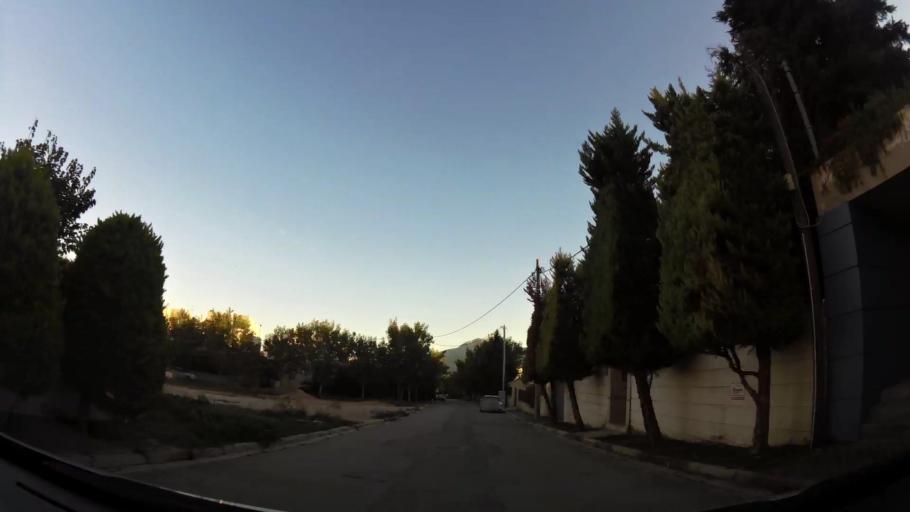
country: GR
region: Attica
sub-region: Nomarchia Anatolikis Attikis
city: Kryoneri
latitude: 38.1438
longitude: 23.8298
